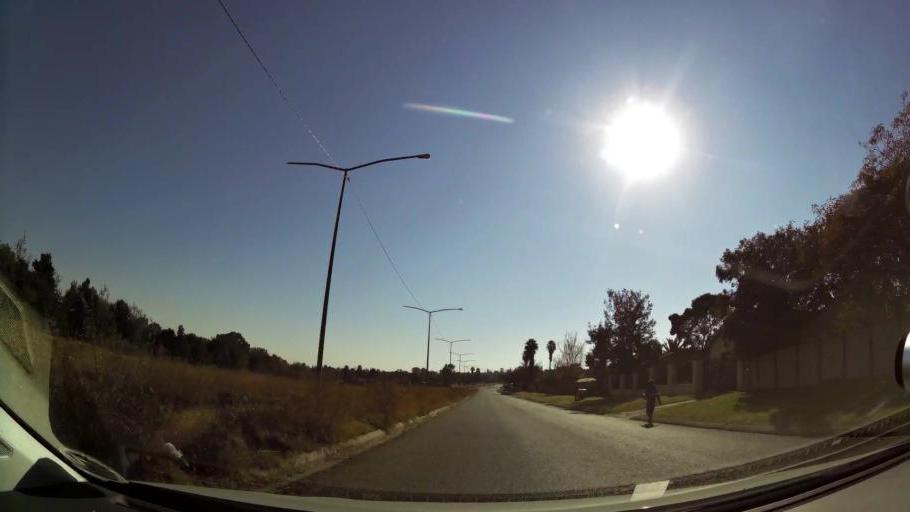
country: ZA
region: Gauteng
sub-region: City of Johannesburg Metropolitan Municipality
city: Modderfontein
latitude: -26.0639
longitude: 28.1976
